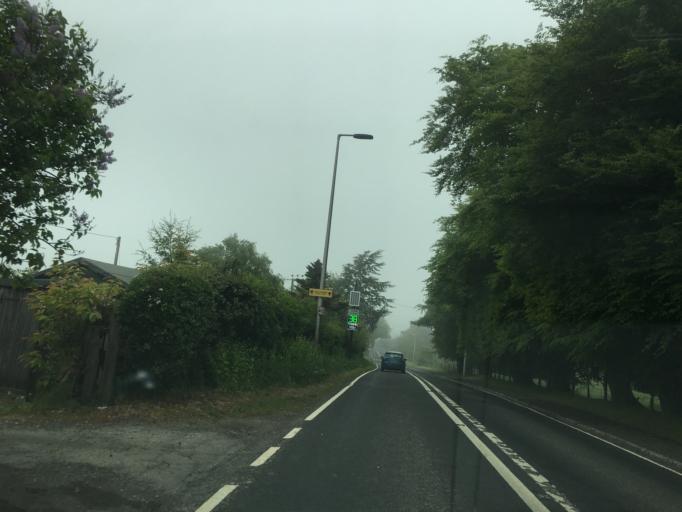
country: GB
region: Scotland
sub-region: Midlothian
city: Penicuik
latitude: 55.8275
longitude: -3.2015
